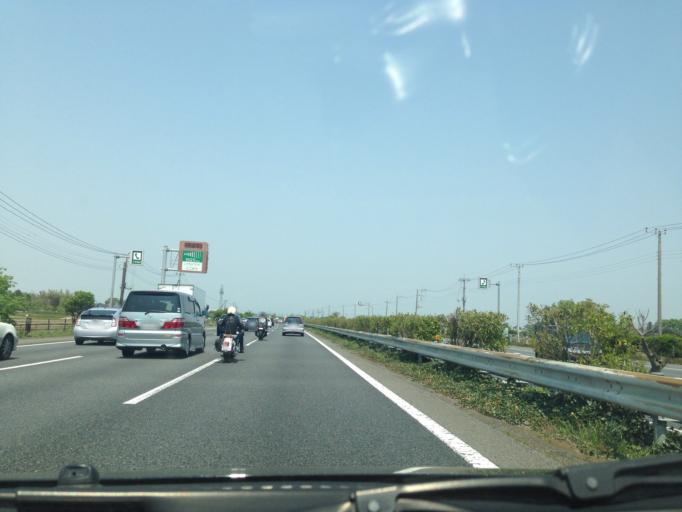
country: JP
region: Saitama
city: Hanyu
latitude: 36.1901
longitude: 139.5839
